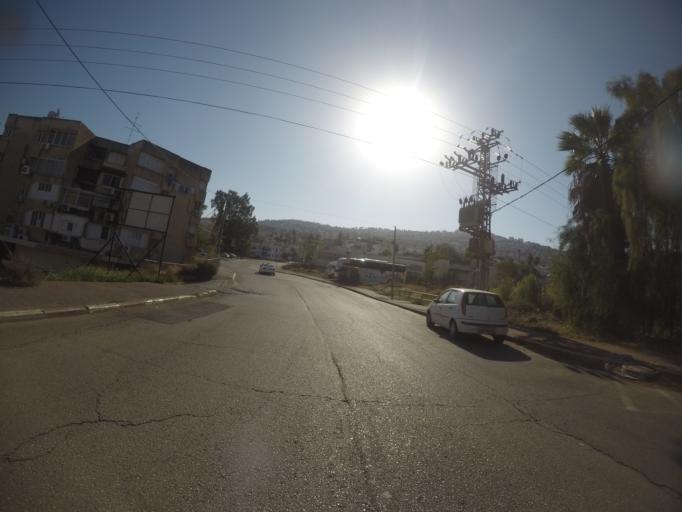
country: IL
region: Northern District
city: Tiberias
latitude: 32.7931
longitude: 35.5260
